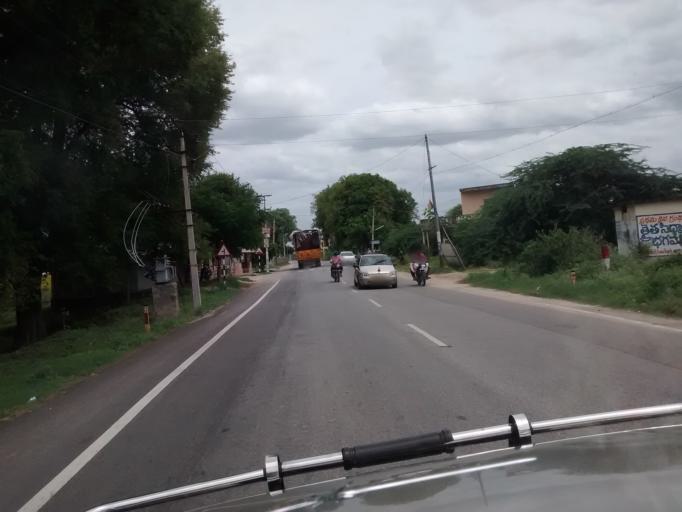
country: IN
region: Andhra Pradesh
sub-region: Chittoor
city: Chittoor
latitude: 13.2869
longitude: 79.0397
